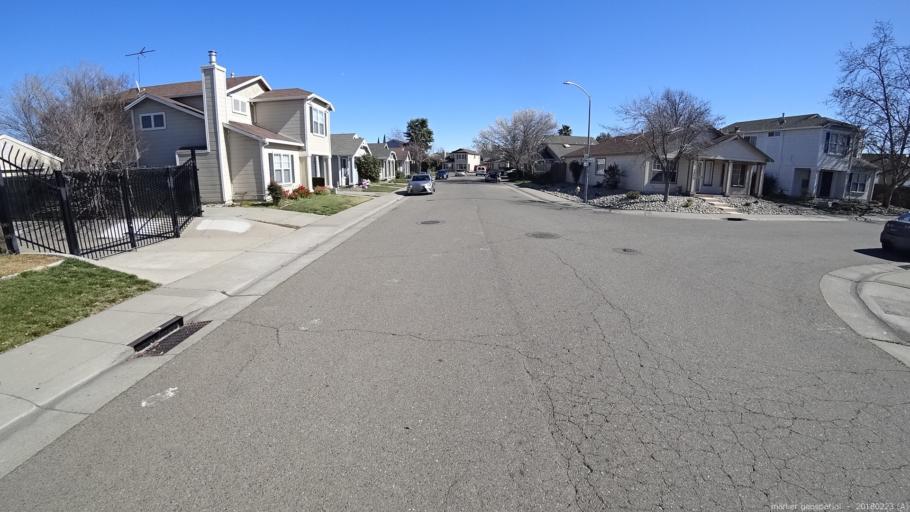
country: US
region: California
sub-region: Sacramento County
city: North Highlands
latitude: 38.7108
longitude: -121.3607
